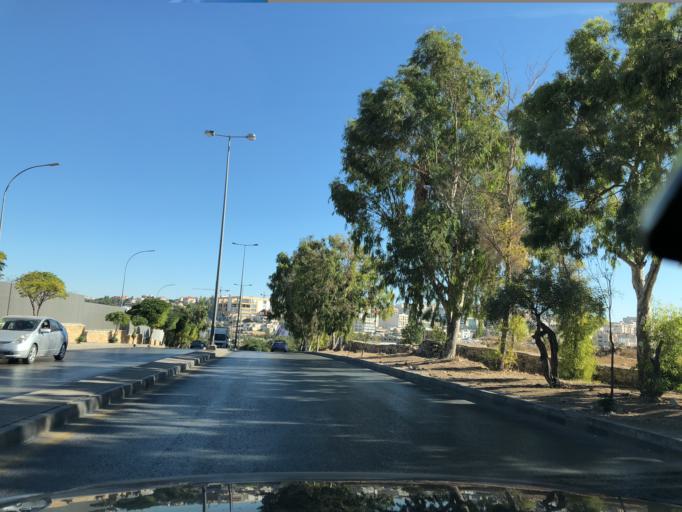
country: JO
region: Amman
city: Wadi as Sir
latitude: 31.9702
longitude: 35.8375
